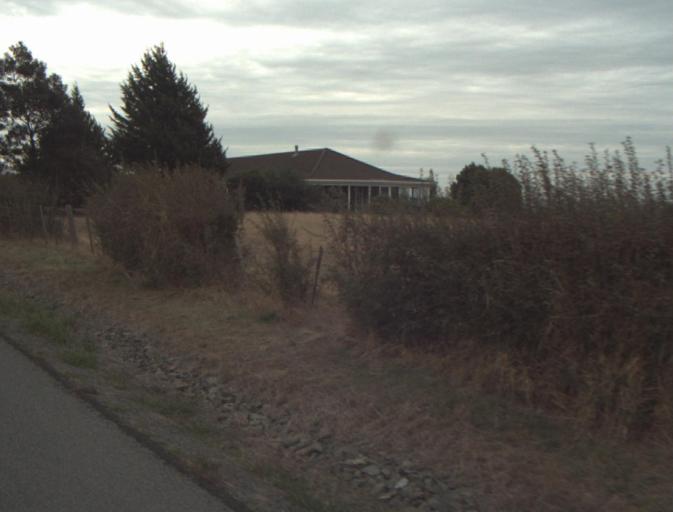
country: AU
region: Tasmania
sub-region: Northern Midlands
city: Evandale
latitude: -41.5171
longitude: 147.2519
